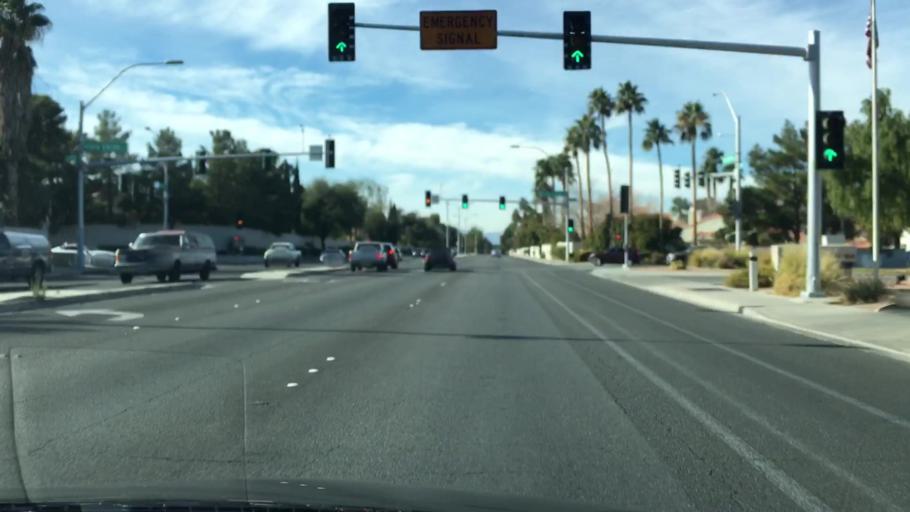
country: US
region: Nevada
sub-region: Clark County
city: Whitney
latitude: 36.0563
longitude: -115.0681
